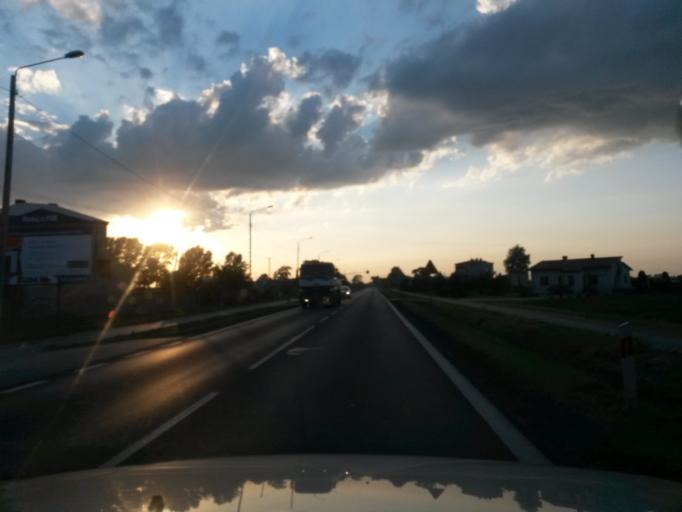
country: PL
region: Lodz Voivodeship
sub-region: Powiat wielunski
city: Wielun
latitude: 51.2415
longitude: 18.5276
